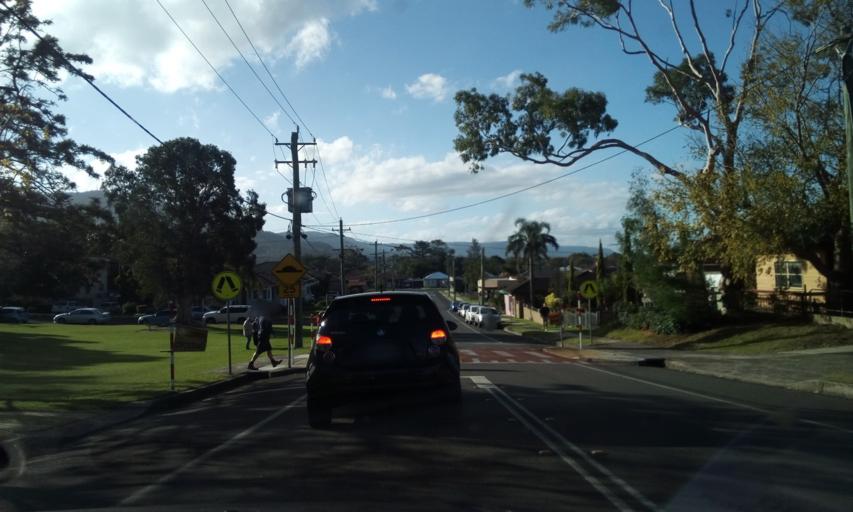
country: AU
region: New South Wales
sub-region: Wollongong
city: Fairy Meadow
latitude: -34.3988
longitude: 150.8869
